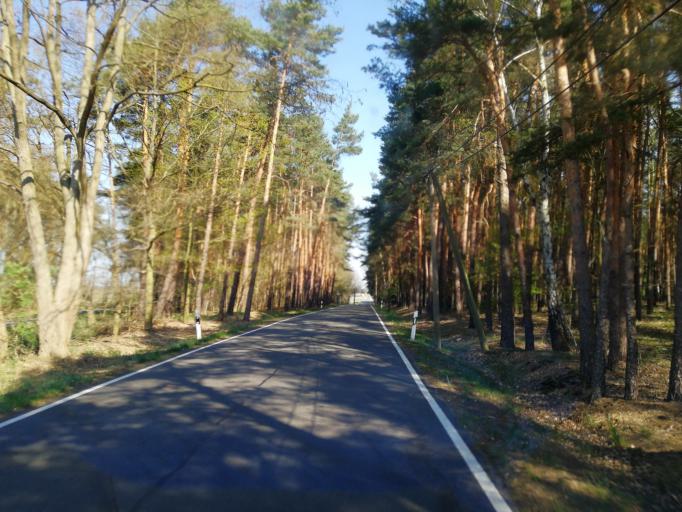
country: DE
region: Brandenburg
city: Bronkow
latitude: 51.7248
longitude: 13.8569
